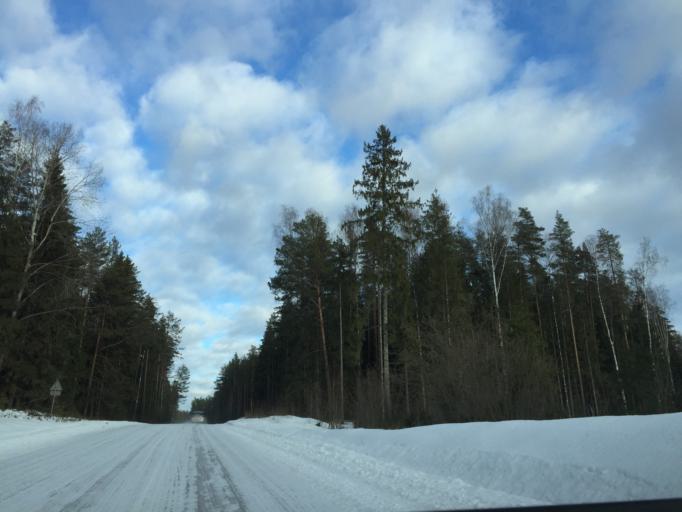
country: LV
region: Ogre
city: Jumprava
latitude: 56.5509
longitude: 24.8959
